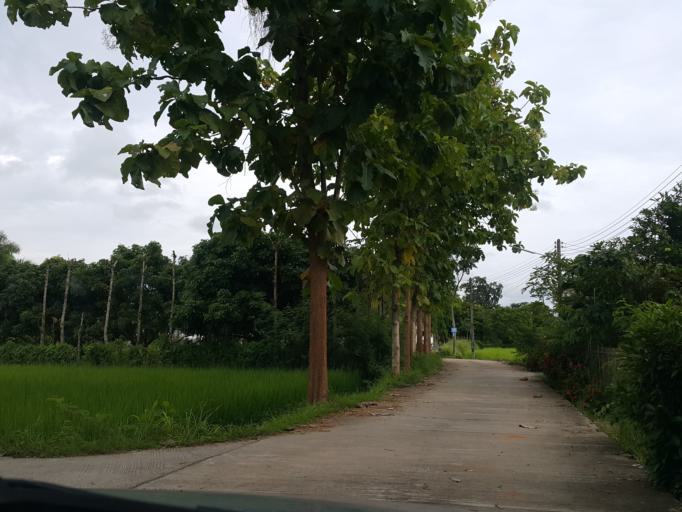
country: TH
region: Chiang Mai
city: San Sai
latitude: 18.8418
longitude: 99.1354
